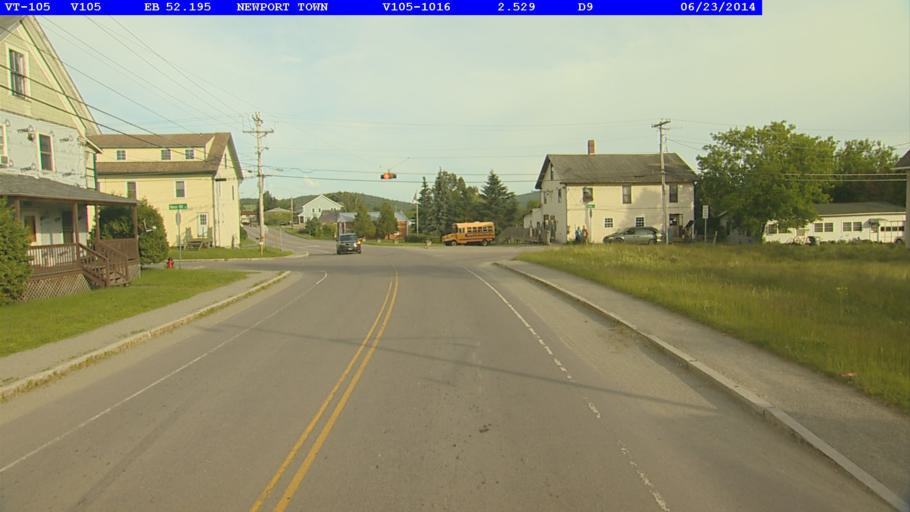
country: US
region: Vermont
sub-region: Orleans County
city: Newport
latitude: 44.9510
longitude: -72.3069
